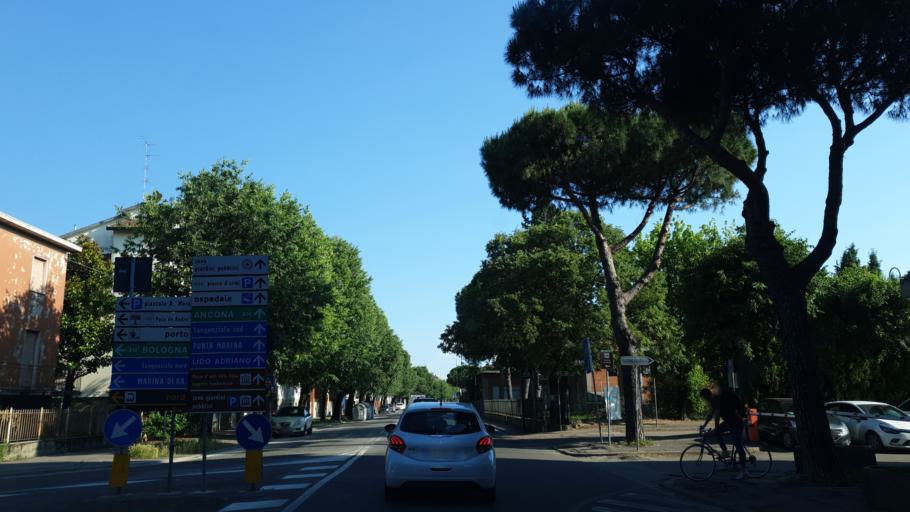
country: IT
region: Emilia-Romagna
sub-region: Provincia di Ravenna
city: Ravenna
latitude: 44.4160
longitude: 12.2104
